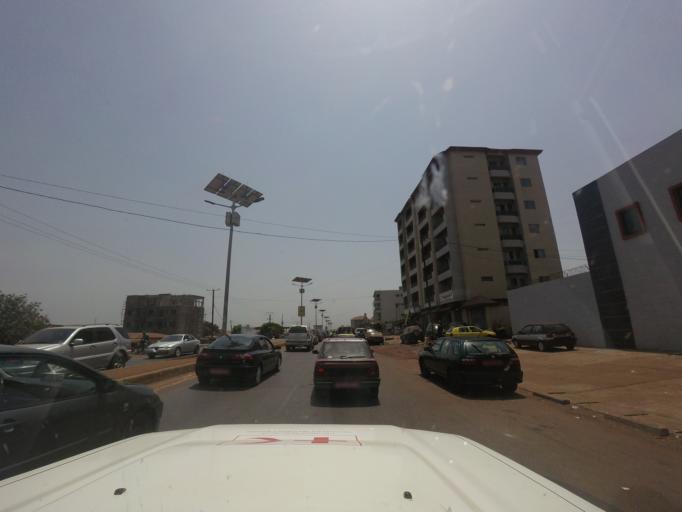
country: GN
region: Conakry
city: Conakry
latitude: 9.6267
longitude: -13.5780
